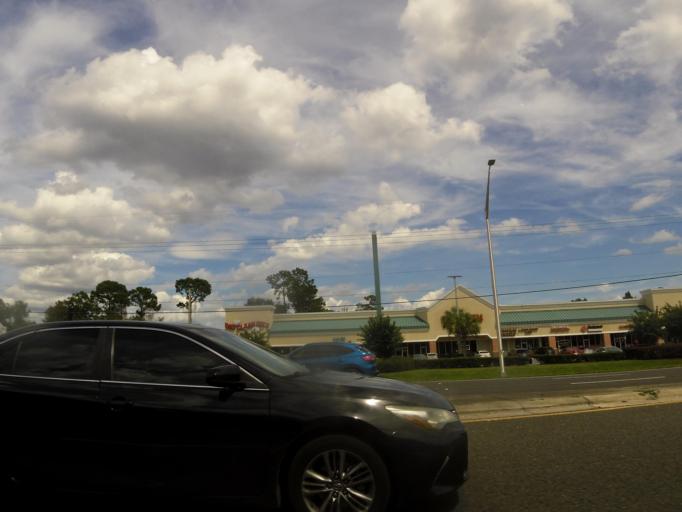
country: US
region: Florida
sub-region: Clay County
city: Orange Park
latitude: 30.1366
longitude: -81.7016
